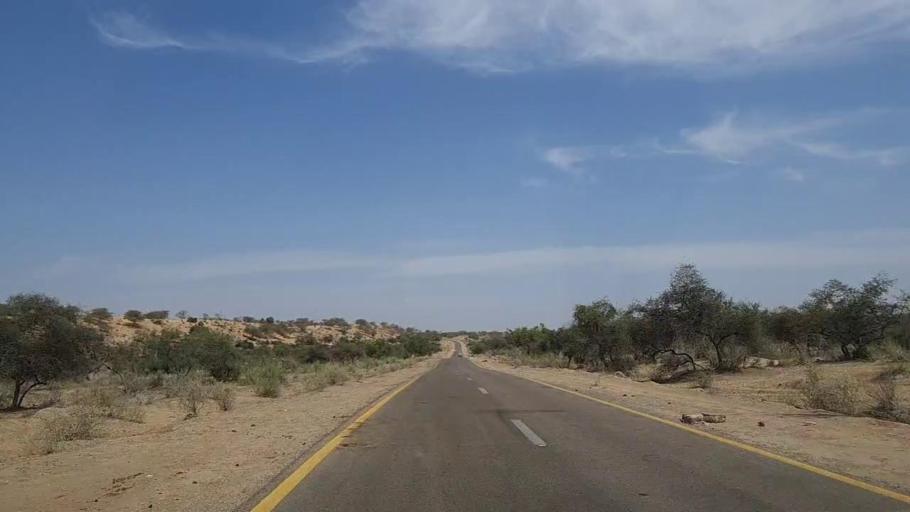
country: PK
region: Sindh
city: Mithi
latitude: 24.8275
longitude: 69.8274
